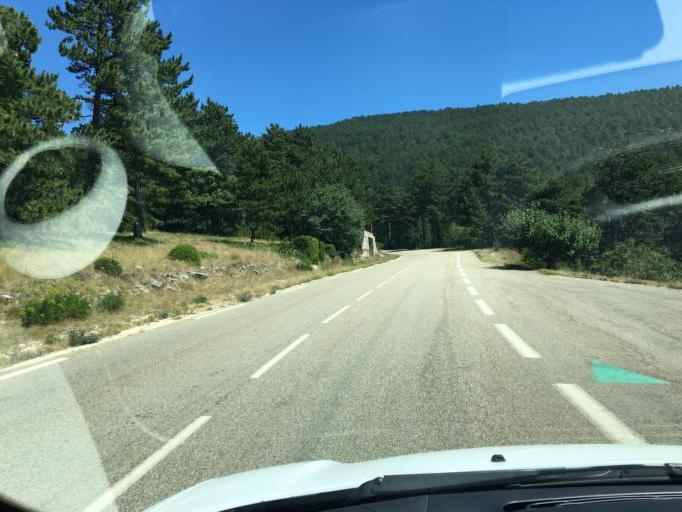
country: FR
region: Provence-Alpes-Cote d'Azur
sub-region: Departement du Vaucluse
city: Bedoin
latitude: 44.1738
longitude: 5.2174
